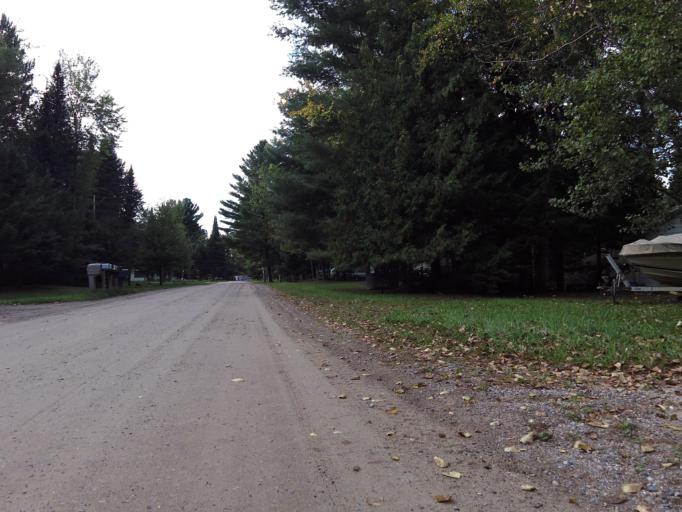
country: US
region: Michigan
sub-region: Roscommon County
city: Saint Helen
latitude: 44.3551
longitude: -84.4882
